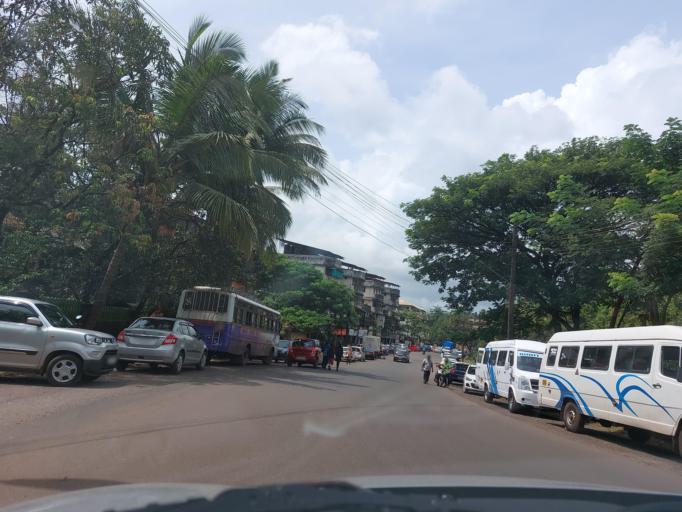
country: IN
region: Goa
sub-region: North Goa
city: Ponda
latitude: 15.4038
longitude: 74.0036
